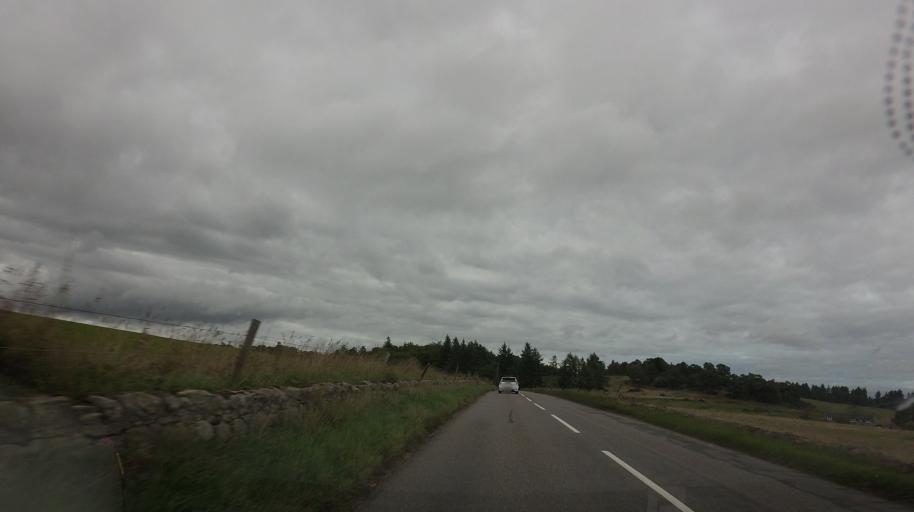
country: GB
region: Scotland
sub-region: Aberdeenshire
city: Kemnay
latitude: 57.1533
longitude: -2.4328
